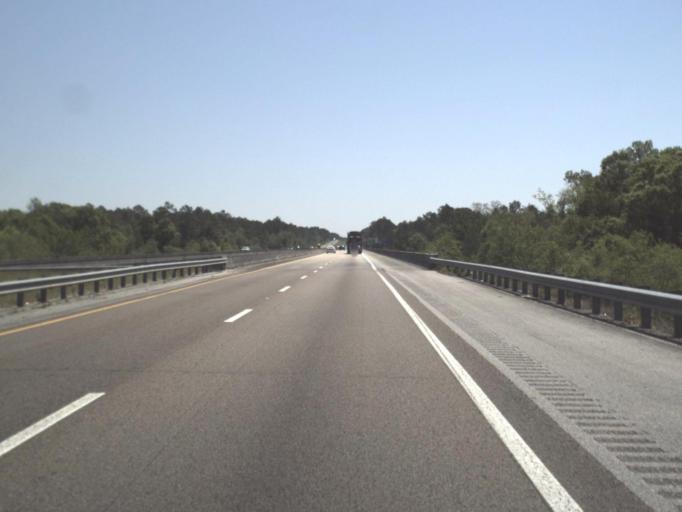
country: US
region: Florida
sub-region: Escambia County
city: Cantonment
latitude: 30.5743
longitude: -87.4147
